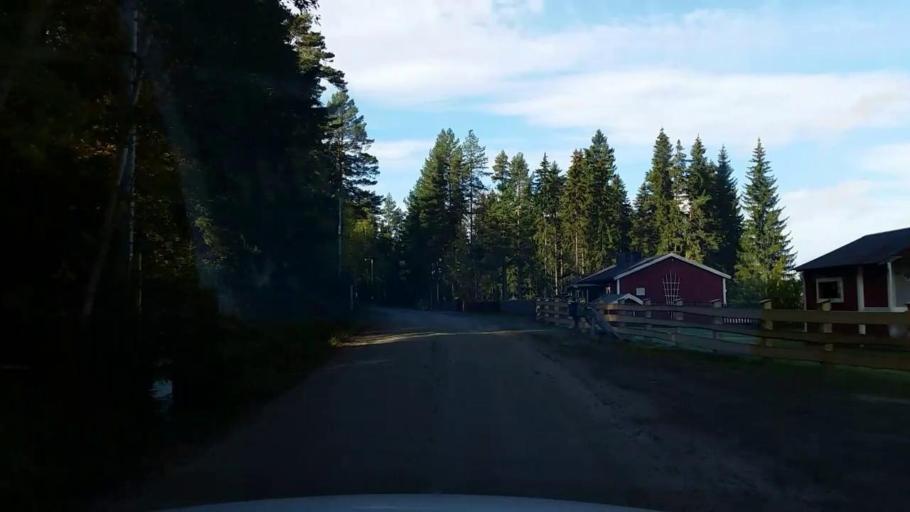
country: SE
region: Gaevleborg
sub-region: Ljusdals Kommun
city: Jaervsoe
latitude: 61.7897
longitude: 16.1954
